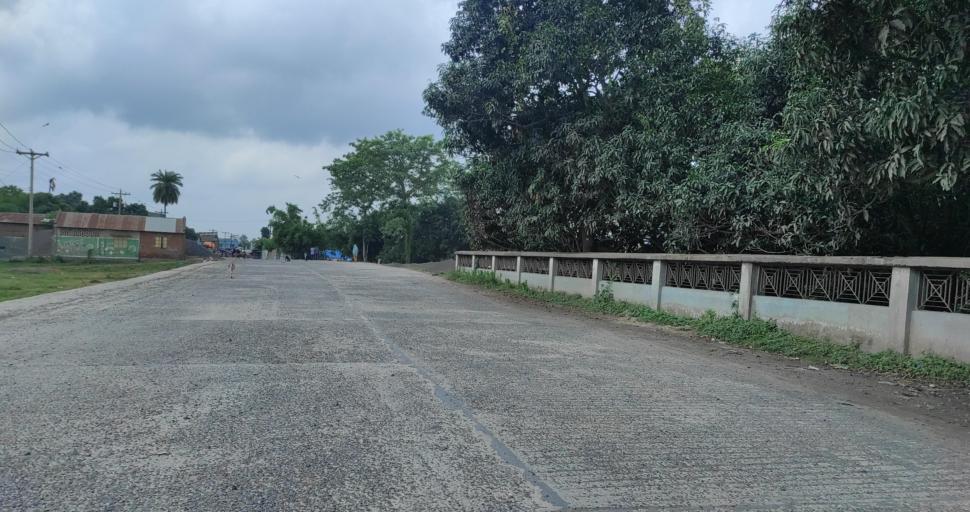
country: BD
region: Rajshahi
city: Shibganj
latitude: 24.8377
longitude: 88.1417
